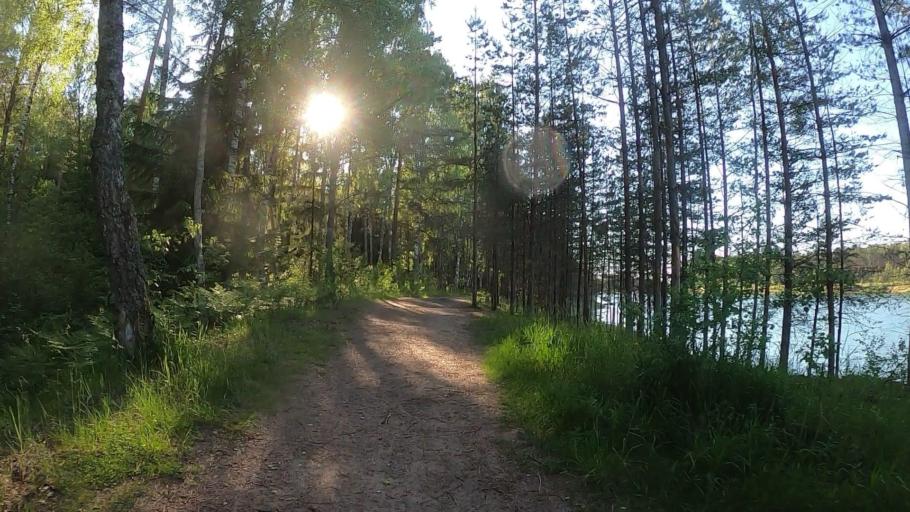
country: LV
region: Ikskile
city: Ikskile
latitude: 56.8390
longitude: 24.5519
